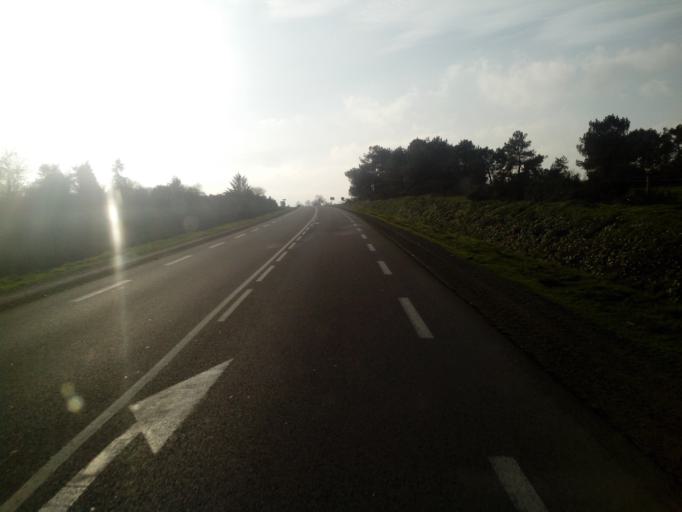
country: FR
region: Brittany
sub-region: Departement du Morbihan
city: Loyat
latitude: 48.0113
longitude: -2.3437
